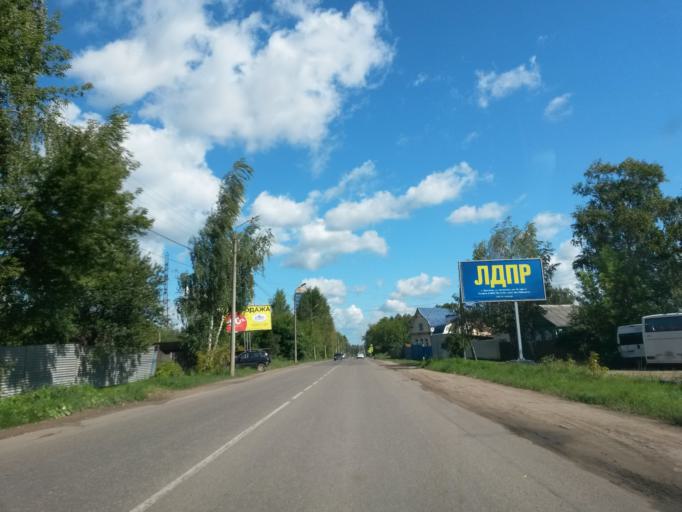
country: RU
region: Jaroslavl
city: Yaroslavl
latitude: 57.5815
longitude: 39.8714
